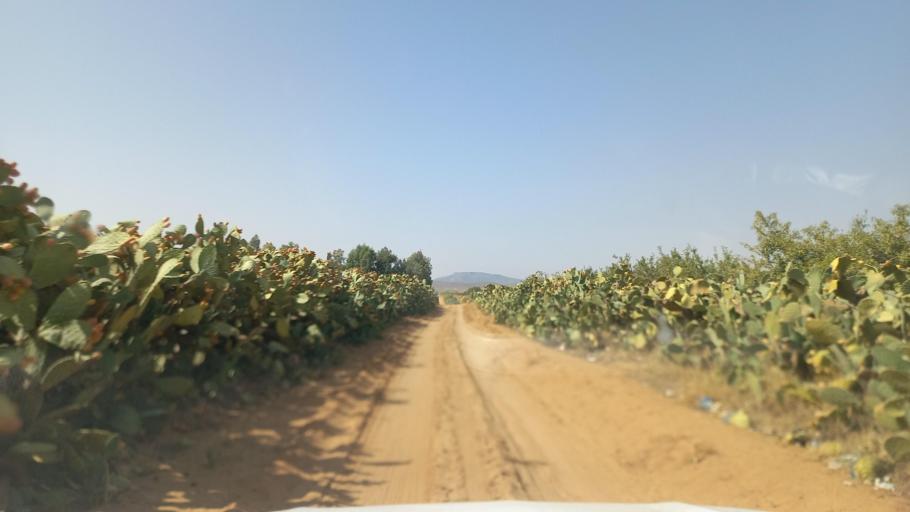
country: TN
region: Al Qasrayn
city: Kasserine
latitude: 35.2347
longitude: 9.0540
